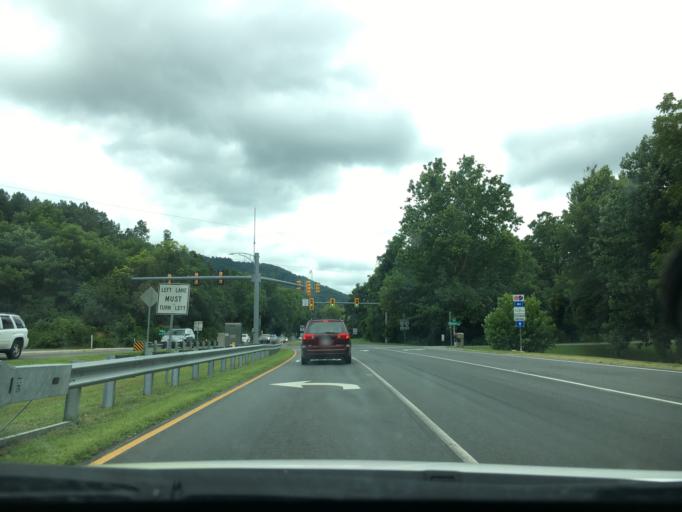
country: US
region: Virginia
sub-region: City of Charlottesville
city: Charlottesville
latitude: 38.0044
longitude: -78.4808
